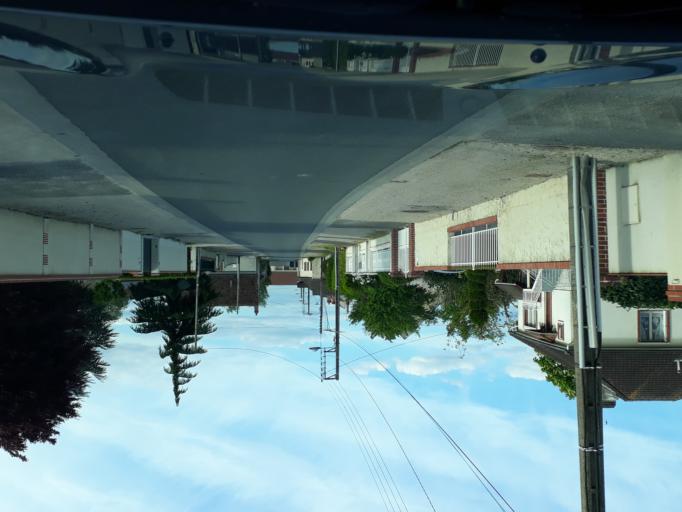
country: FR
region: Centre
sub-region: Departement du Loiret
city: Ingre
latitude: 47.9129
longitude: 1.8410
